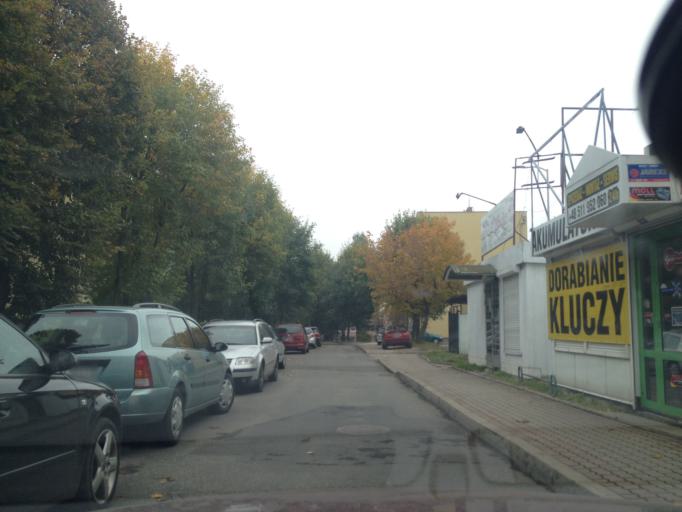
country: PL
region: Lower Silesian Voivodeship
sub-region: Powiat zgorzelecki
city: Zgorzelec
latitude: 51.1560
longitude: 15.0140
